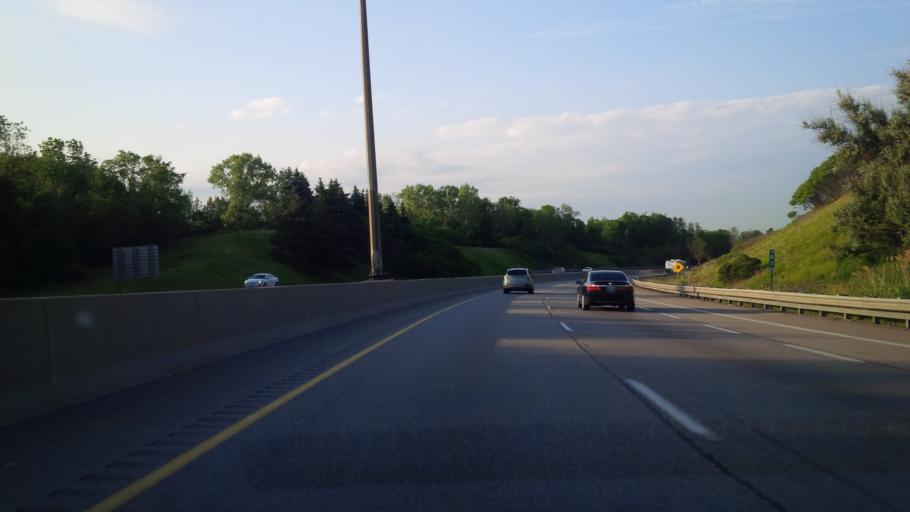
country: CA
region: Ontario
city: Ancaster
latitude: 43.2400
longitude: -79.9483
